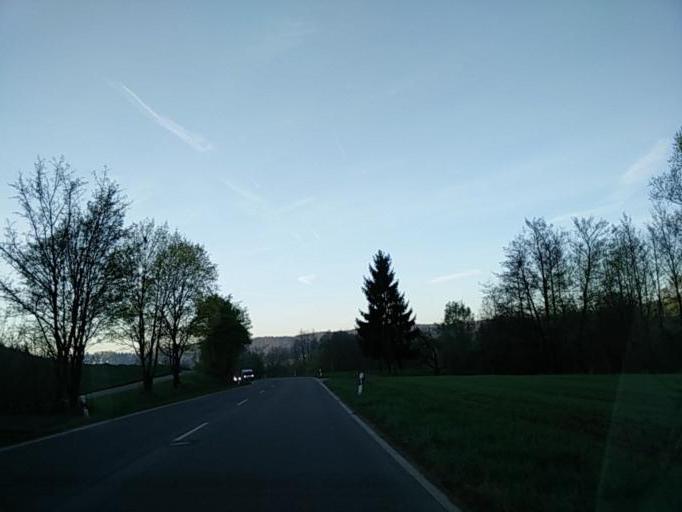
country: DE
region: Baden-Wuerttemberg
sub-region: Tuebingen Region
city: Tuebingen
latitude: 48.5331
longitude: 9.0217
